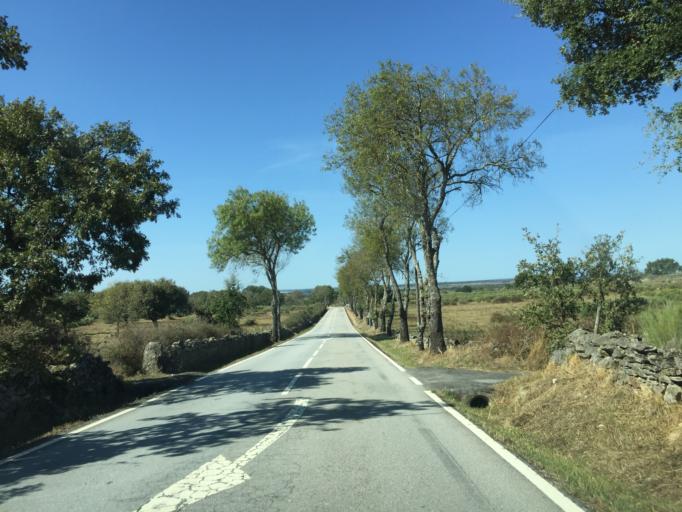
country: PT
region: Portalegre
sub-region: Portalegre
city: Alagoa
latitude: 39.4393
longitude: -7.5575
